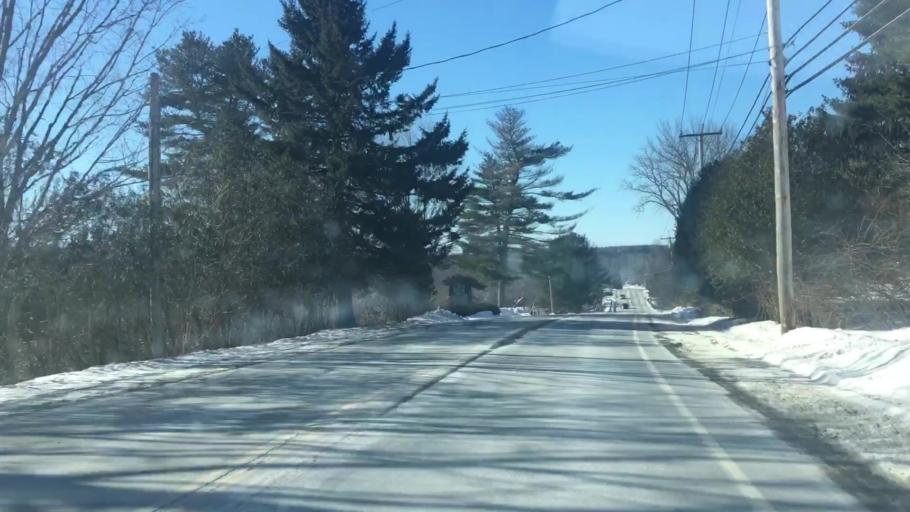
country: US
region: Maine
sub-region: Hancock County
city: Surry
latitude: 44.4958
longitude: -68.4979
